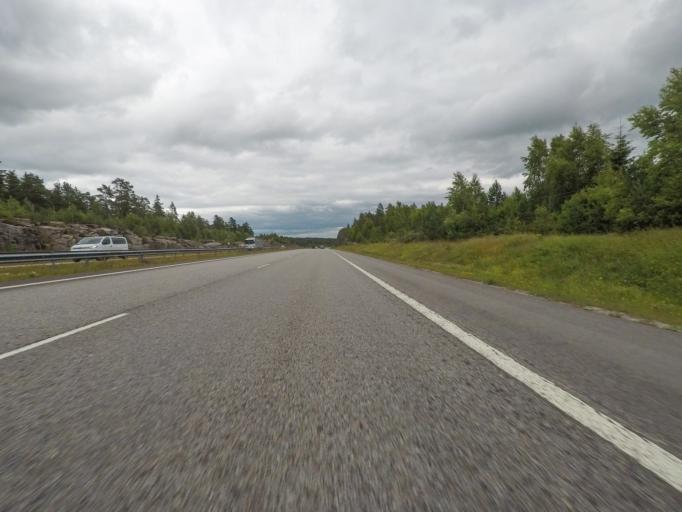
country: FI
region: Varsinais-Suomi
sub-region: Salo
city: Halikko
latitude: 60.4350
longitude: 22.9669
